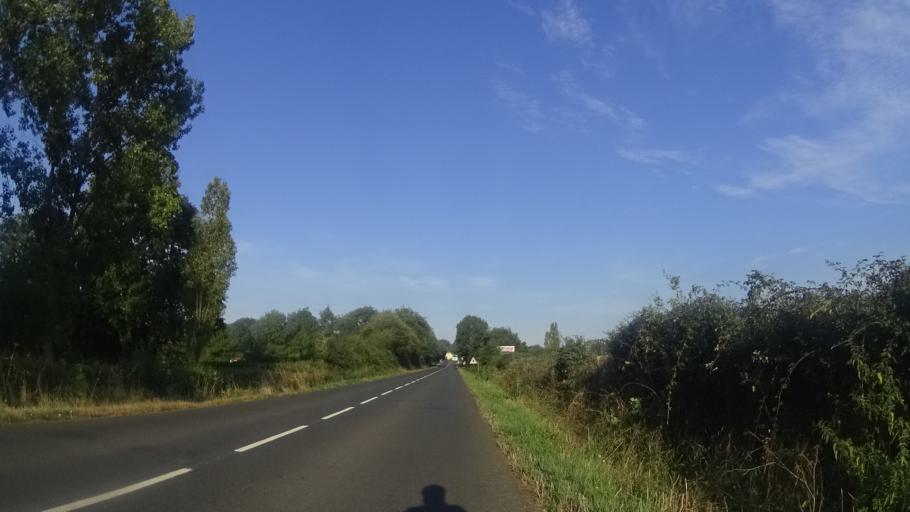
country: FR
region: Pays de la Loire
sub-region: Departement de la Loire-Atlantique
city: Riaille
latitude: 47.5148
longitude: -1.2792
